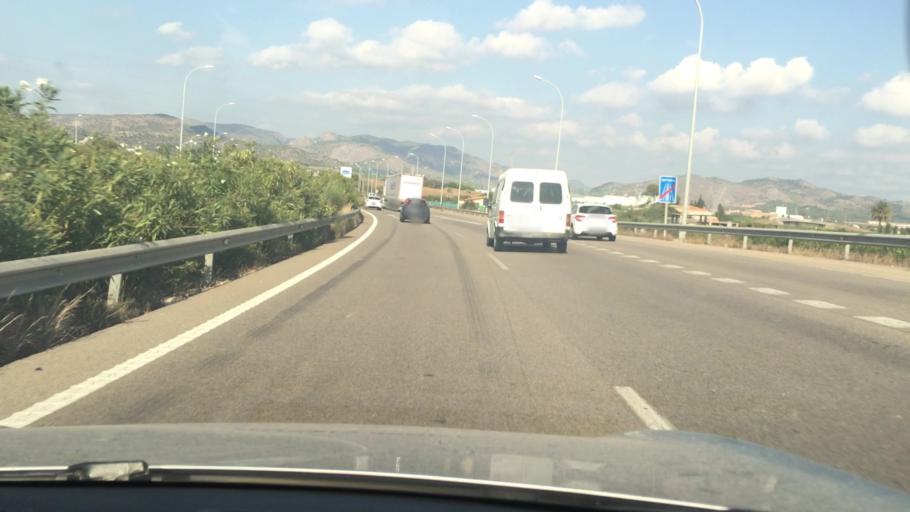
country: ES
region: Valencia
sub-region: Provincia de Castello
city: Vila-real
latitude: 39.9870
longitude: -0.1233
